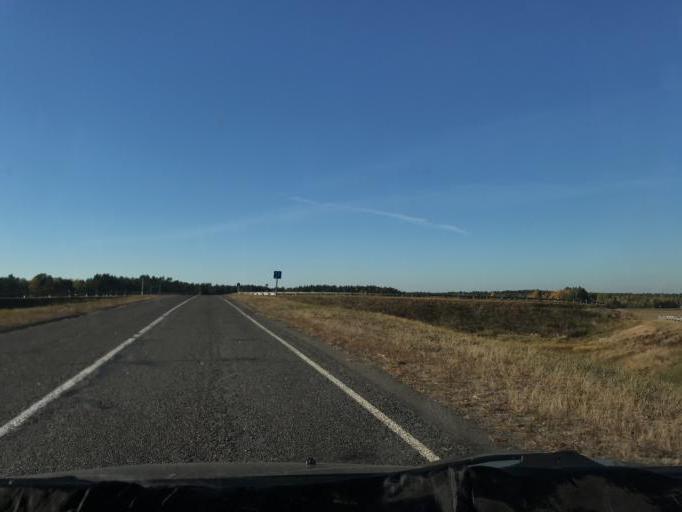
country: BY
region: Gomel
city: Kalinkavichy
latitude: 52.0720
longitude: 29.3642
